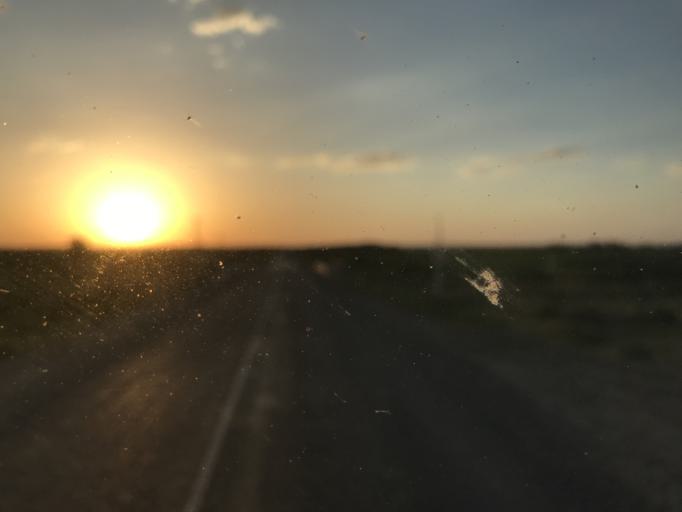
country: UZ
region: Toshkent
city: Yangiyul
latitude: 41.3815
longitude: 68.7759
